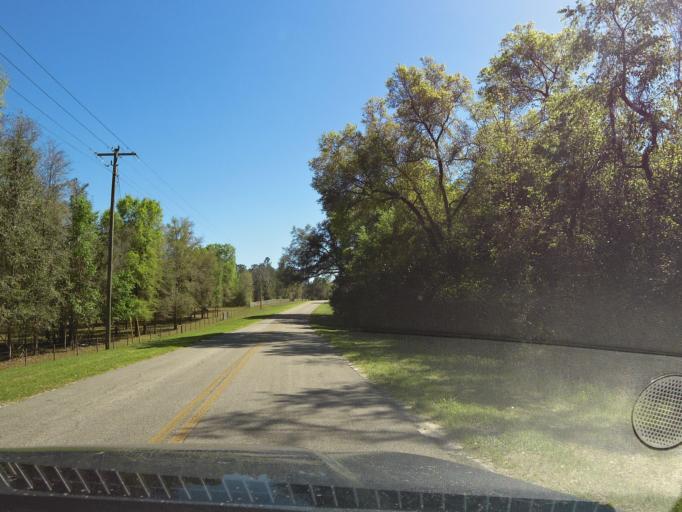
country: US
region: Florida
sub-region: Clay County
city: Keystone Heights
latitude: 29.8202
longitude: -82.0579
